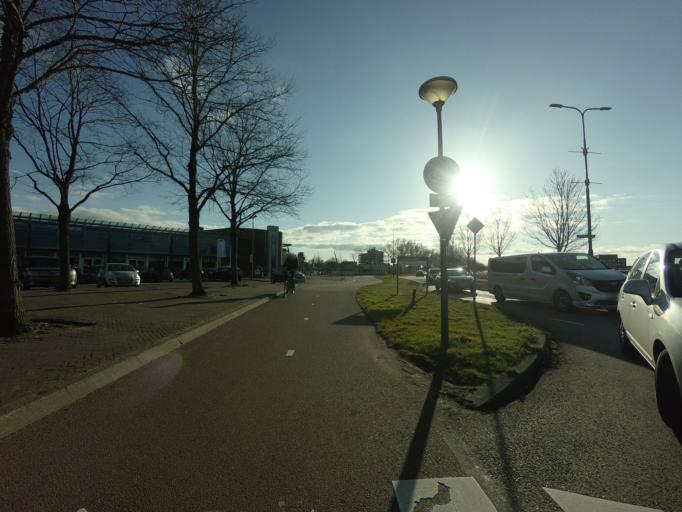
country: NL
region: Utrecht
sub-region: Gemeente Woerden
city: Woerden
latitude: 52.0873
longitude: 4.9035
